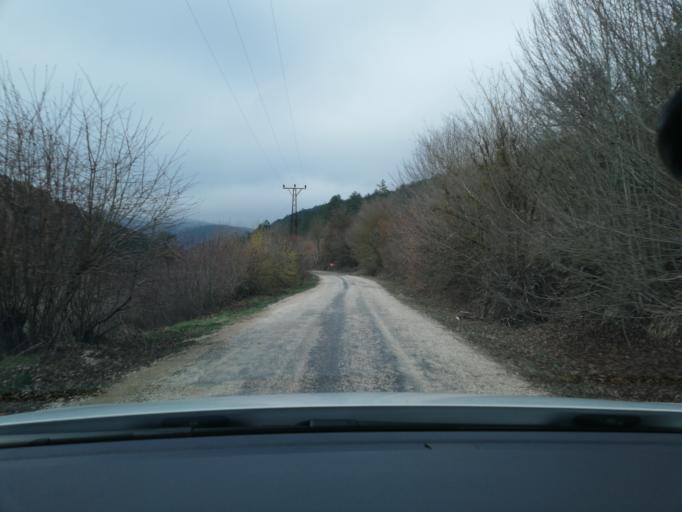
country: TR
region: Bolu
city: Bolu
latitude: 40.6851
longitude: 31.4661
